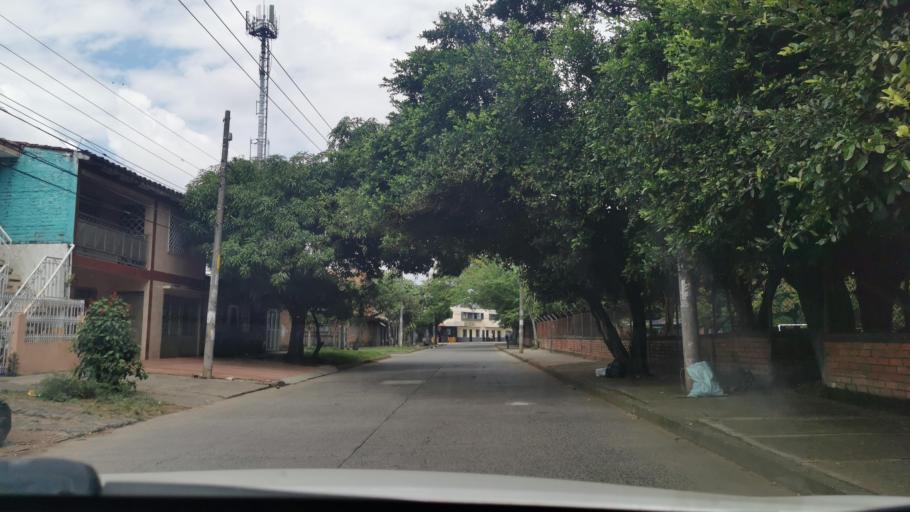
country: CO
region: Valle del Cauca
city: Jamundi
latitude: 3.2665
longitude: -76.5407
